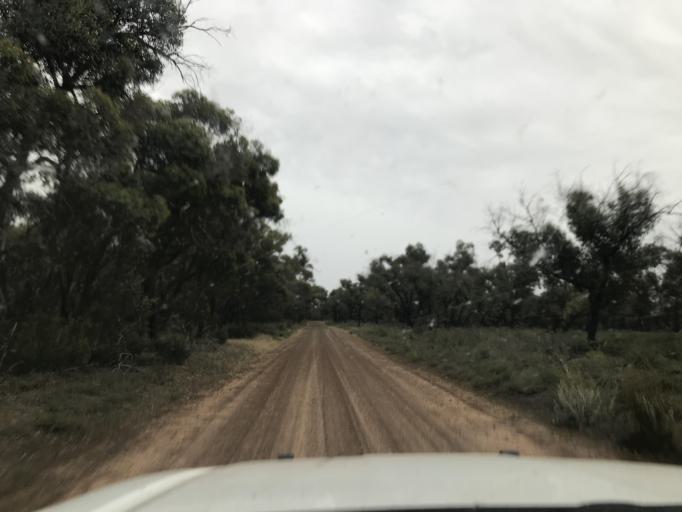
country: AU
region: South Australia
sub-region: Wattle Range
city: Penola
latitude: -37.0934
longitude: 141.5050
